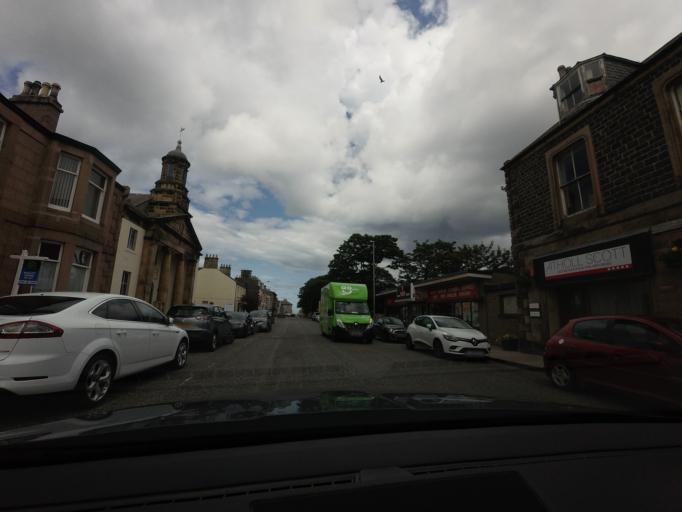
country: GB
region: Scotland
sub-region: Aberdeenshire
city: Banff
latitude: 57.6656
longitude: -2.5236
